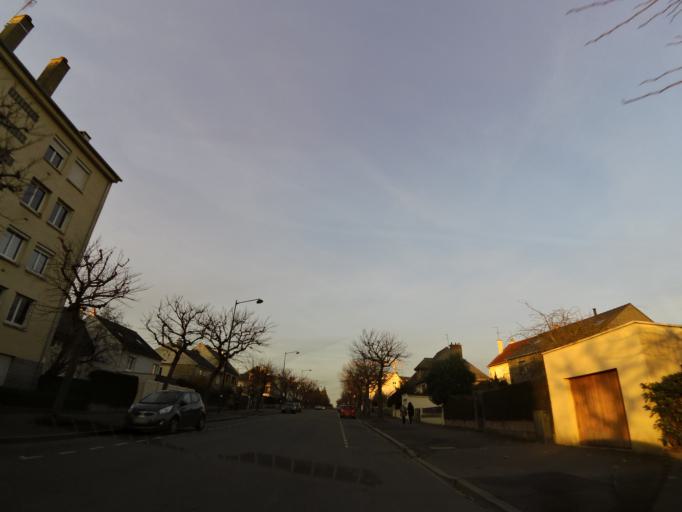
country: FR
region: Brittany
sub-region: Departement d'Ille-et-Vilaine
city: Rennes
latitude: 48.1188
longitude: -1.6554
